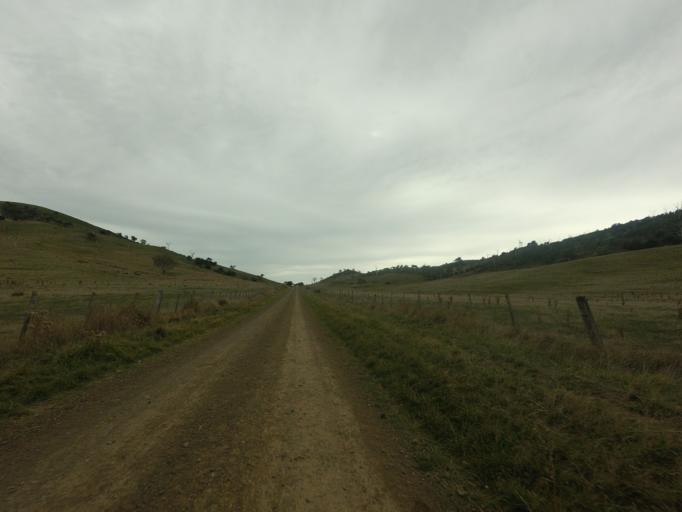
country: AU
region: Tasmania
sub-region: Derwent Valley
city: New Norfolk
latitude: -42.3788
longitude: 146.8663
